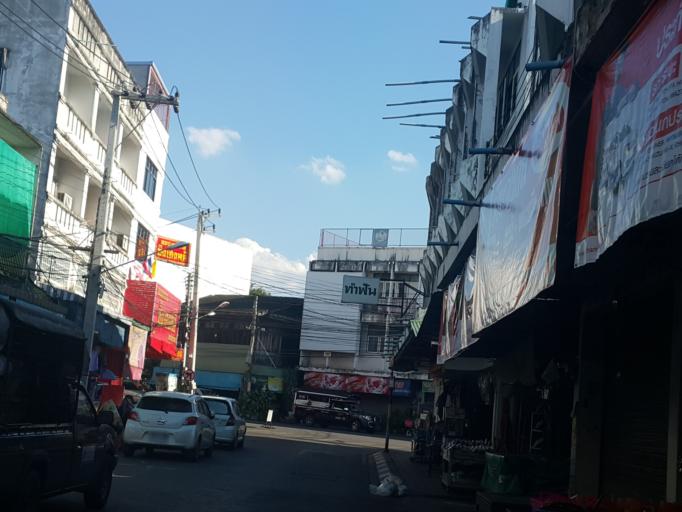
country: TH
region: Lampang
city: Lampang
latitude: 18.2883
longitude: 99.5016
